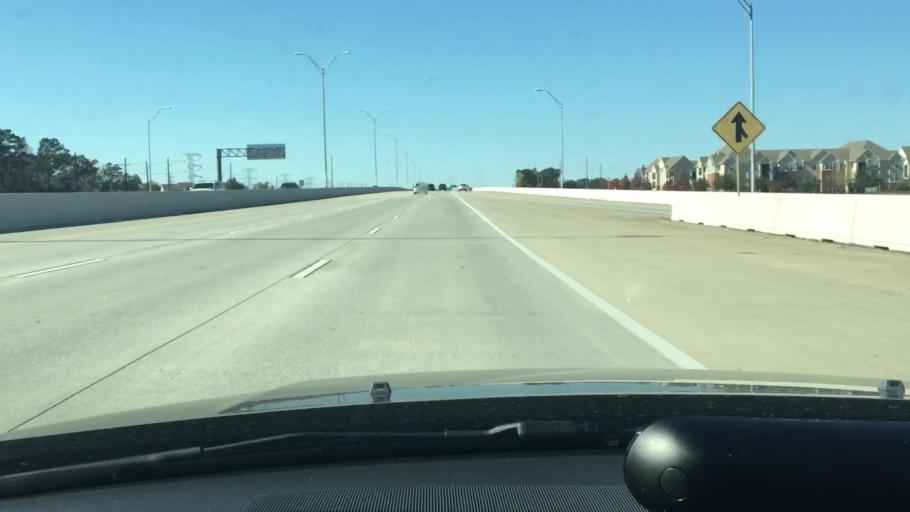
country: US
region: Texas
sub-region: Harris County
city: Humble
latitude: 29.9343
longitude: -95.2303
